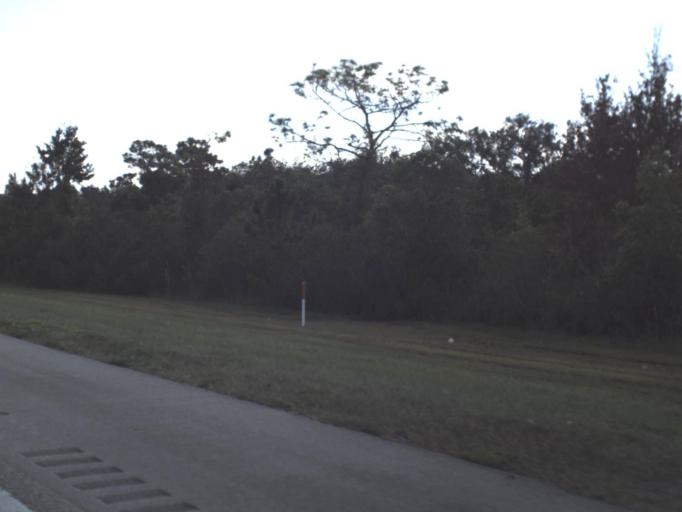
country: US
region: Florida
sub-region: Indian River County
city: Fellsmere
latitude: 27.7368
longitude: -80.9232
